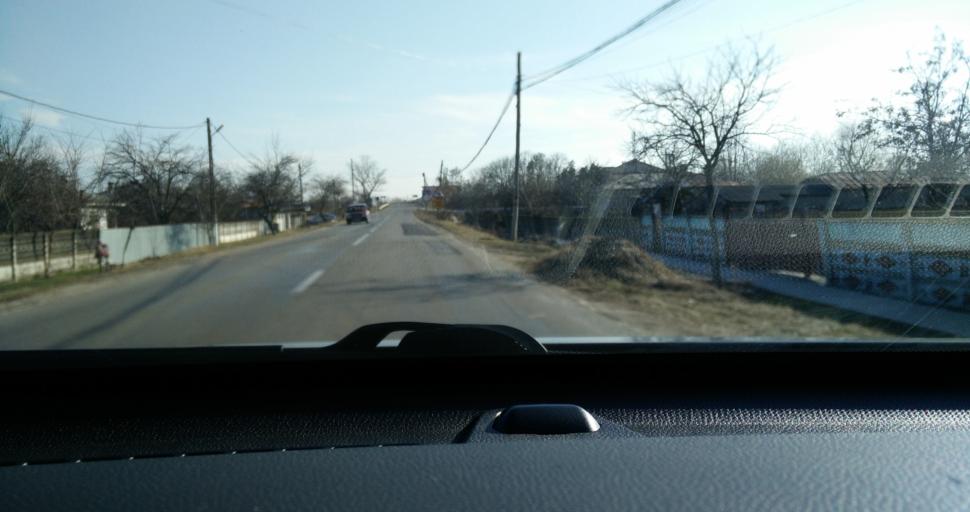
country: RO
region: Vrancea
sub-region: Comuna Maicanesti
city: Maicanesti
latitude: 45.5055
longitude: 27.4856
